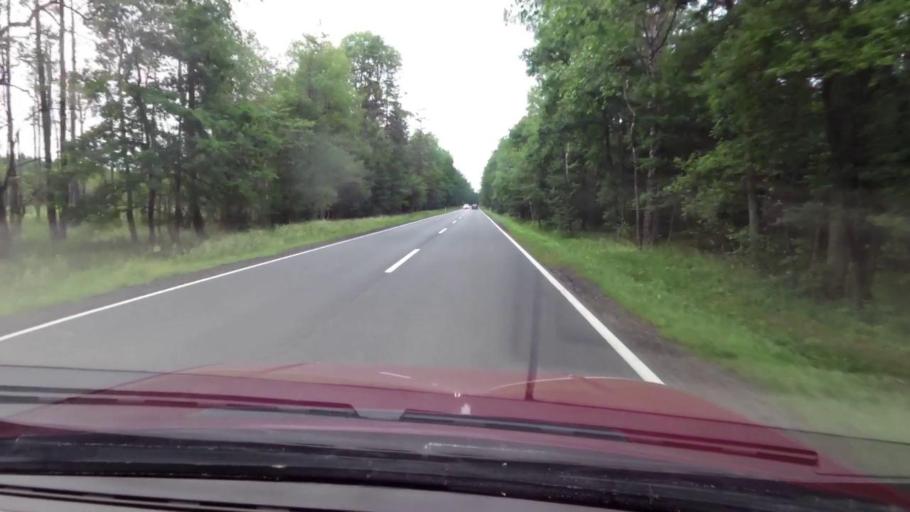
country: PL
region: Pomeranian Voivodeship
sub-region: Powiat bytowski
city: Trzebielino
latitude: 54.2253
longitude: 17.0872
